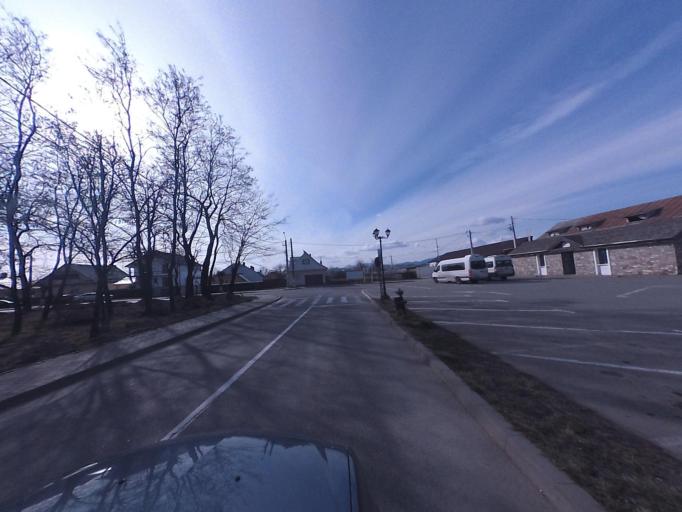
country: RO
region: Neamt
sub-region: Oras Targu Neamt
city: Humulesti
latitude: 47.2105
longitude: 26.3451
